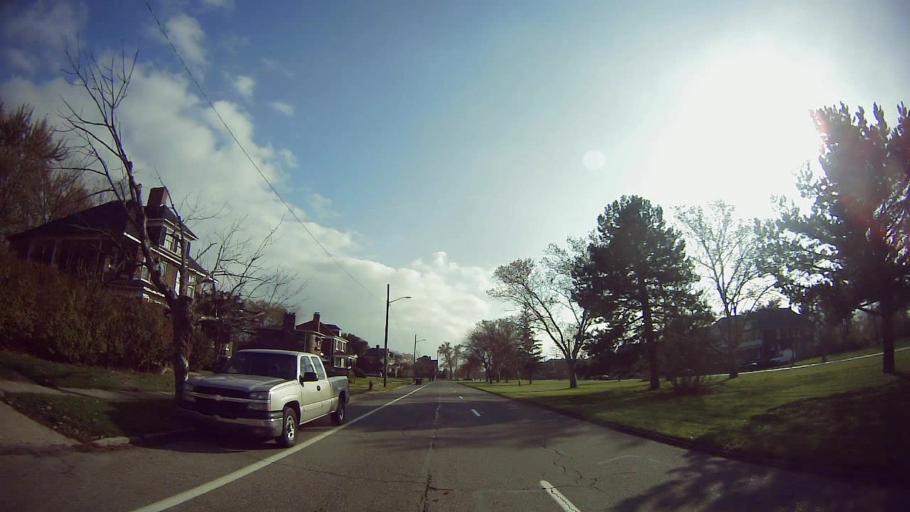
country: US
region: Michigan
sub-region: Wayne County
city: Detroit
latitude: 42.3433
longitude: -83.1065
